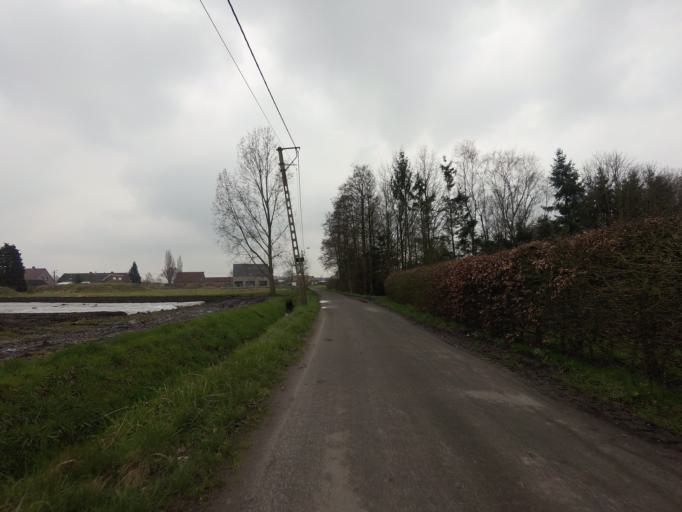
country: BE
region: Flanders
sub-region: Provincie Antwerpen
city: Putte
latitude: 51.0663
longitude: 4.5987
